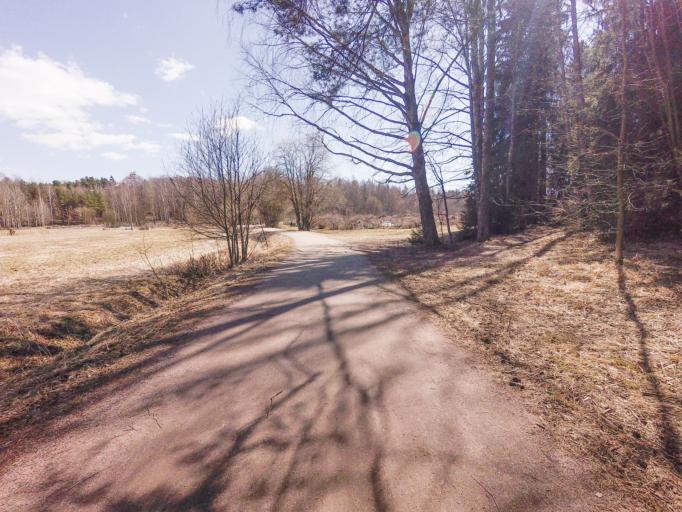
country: FI
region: Uusimaa
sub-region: Helsinki
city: Vantaa
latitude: 60.2117
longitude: 25.0270
